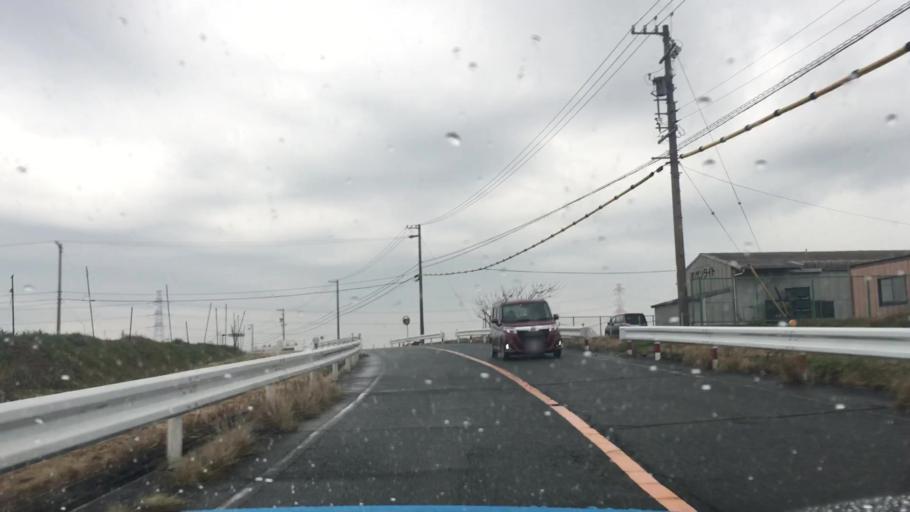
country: JP
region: Aichi
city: Toyohashi
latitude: 34.6804
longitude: 137.3897
